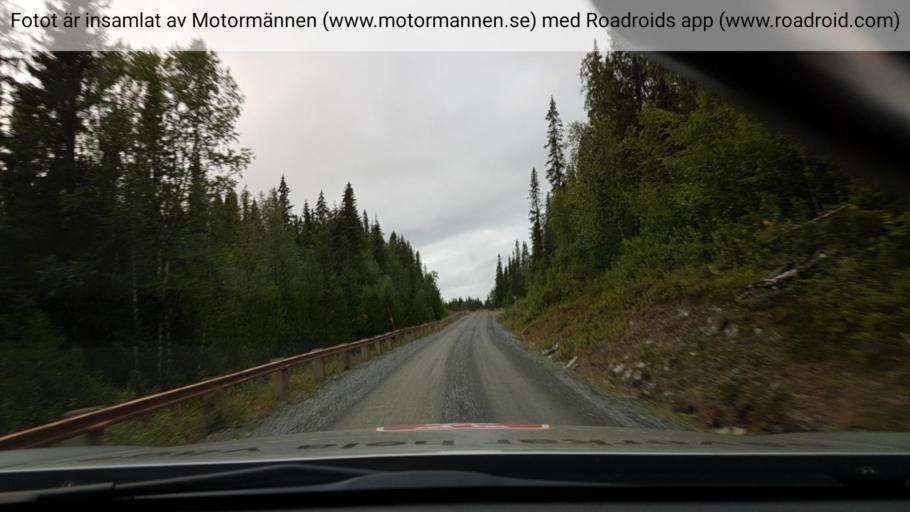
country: SE
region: Vaesterbotten
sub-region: Vilhelmina Kommun
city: Sjoberg
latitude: 65.5335
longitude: 15.4343
